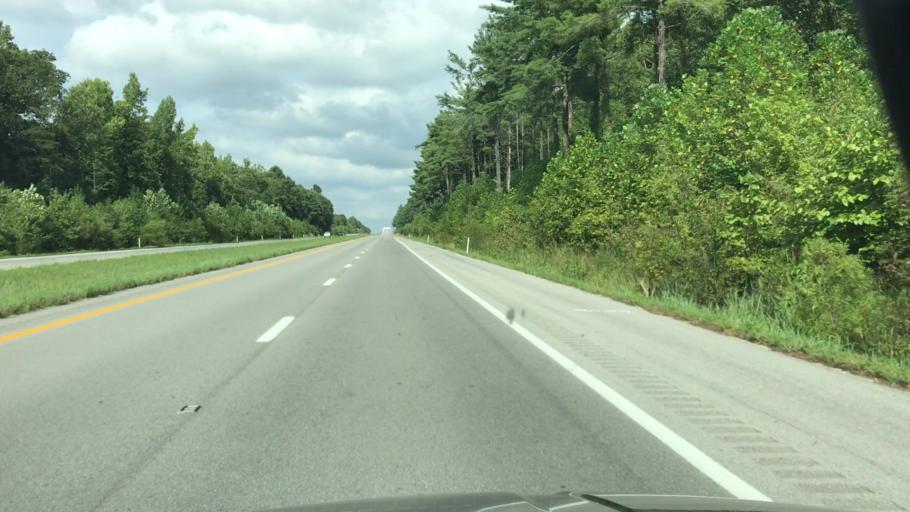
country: US
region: Kentucky
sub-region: Hopkins County
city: Dawson Springs
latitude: 37.1824
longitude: -87.7244
